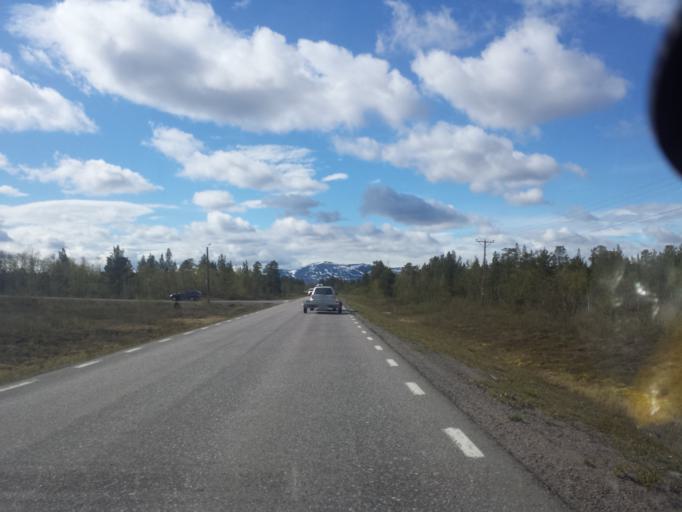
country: SE
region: Norrbotten
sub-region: Kiruna Kommun
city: Kiruna
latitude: 67.9925
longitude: 19.9149
